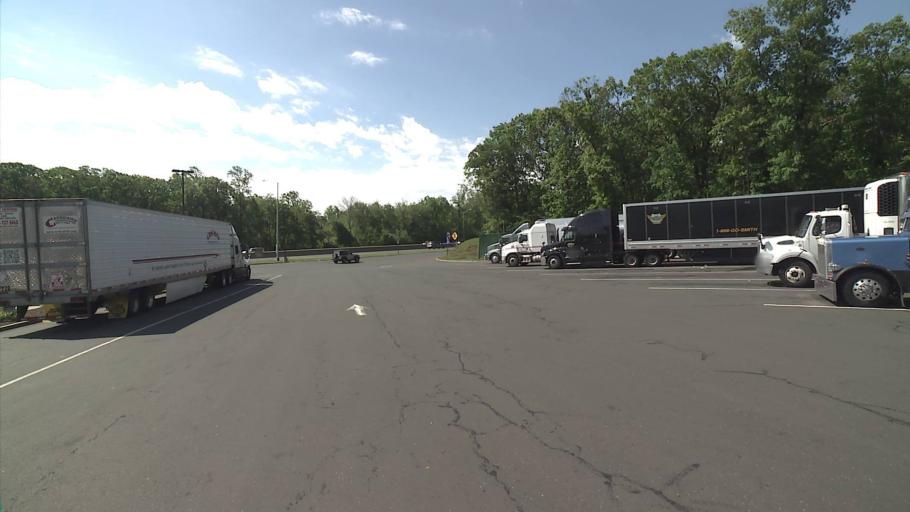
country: US
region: Connecticut
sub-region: New Haven County
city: Woodmont
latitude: 41.2462
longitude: -73.0111
